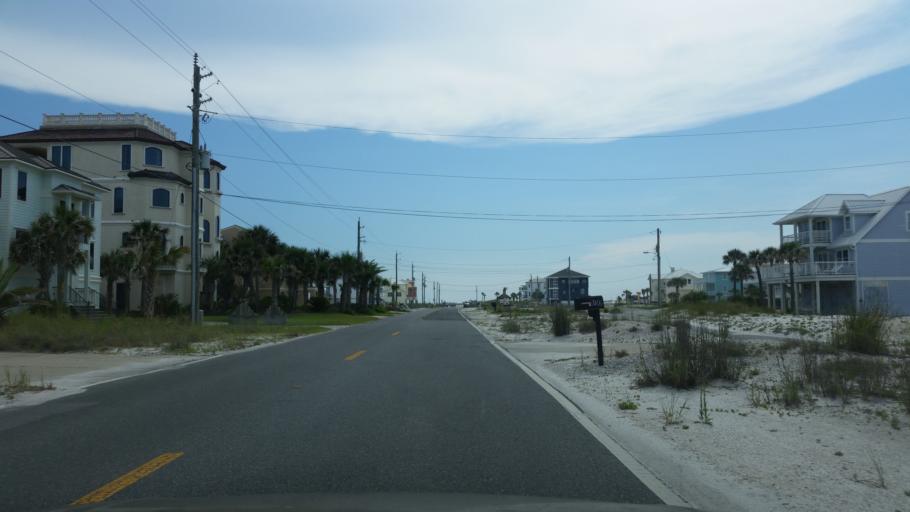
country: US
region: Florida
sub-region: Santa Rosa County
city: Navarre
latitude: 30.3725
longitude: -86.9142
